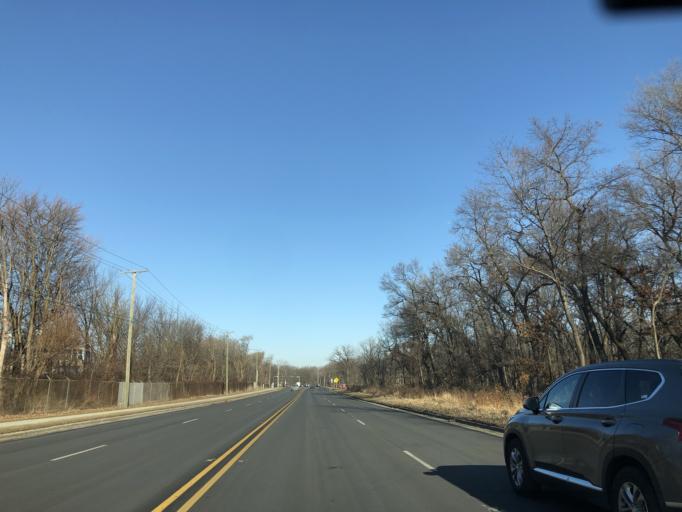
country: US
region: Illinois
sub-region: Cook County
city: Riverside
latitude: 41.8318
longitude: -87.8291
